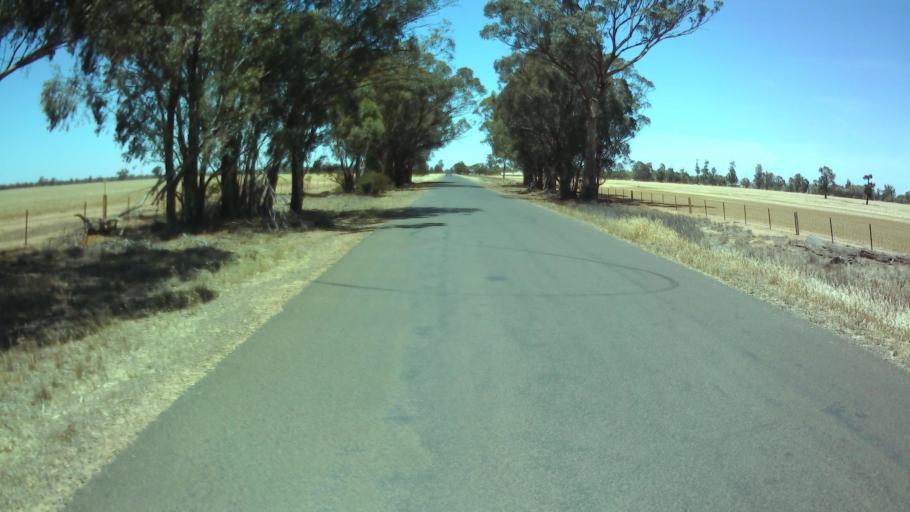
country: AU
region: New South Wales
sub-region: Weddin
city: Grenfell
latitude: -34.0244
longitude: 147.7919
